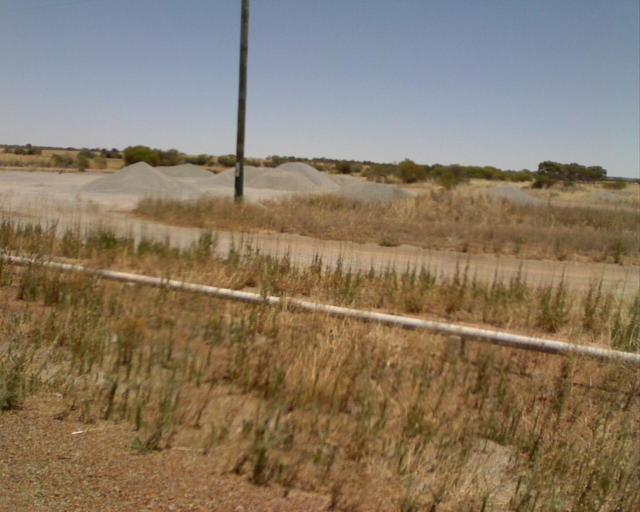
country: AU
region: Western Australia
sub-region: Merredin
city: Merredin
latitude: -30.8323
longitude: 117.8624
